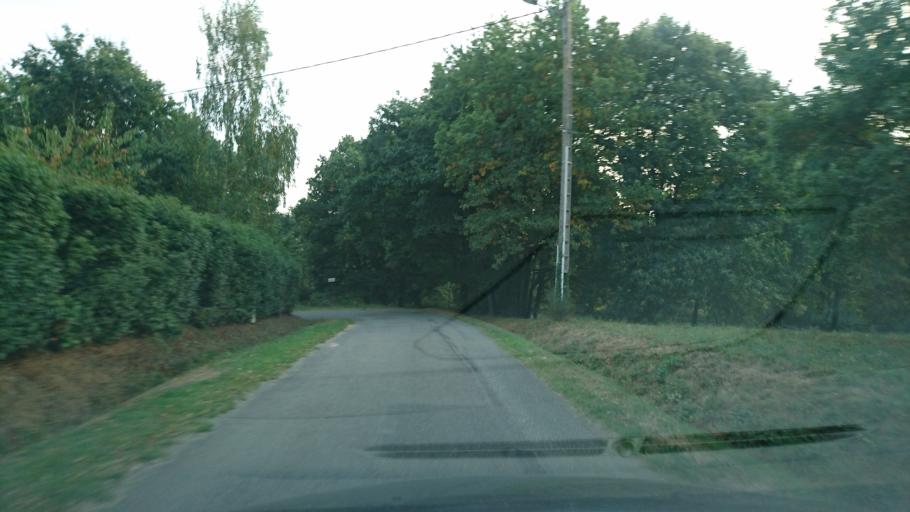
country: FR
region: Brittany
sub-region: Departement du Morbihan
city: Saint-Vincent-sur-Oust
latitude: 47.6985
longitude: -2.1505
